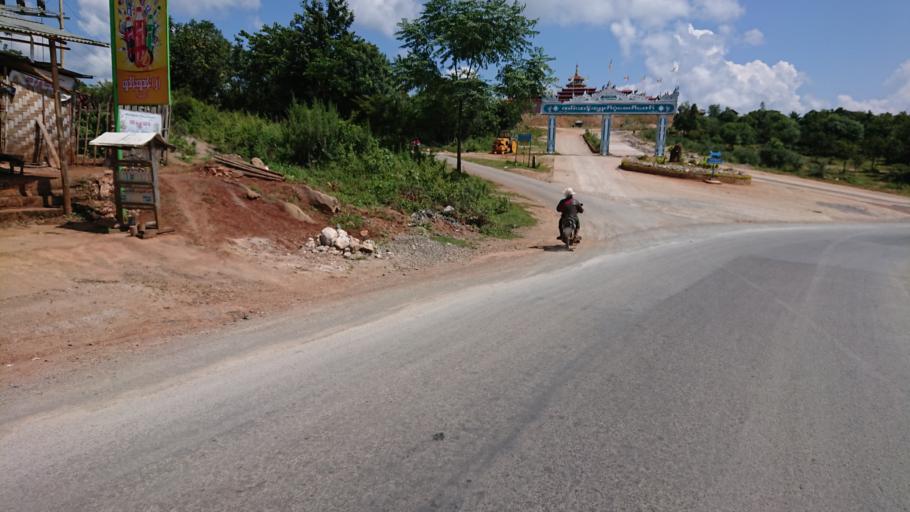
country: MM
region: Shan
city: Taunggyi
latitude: 20.8151
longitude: 97.3267
